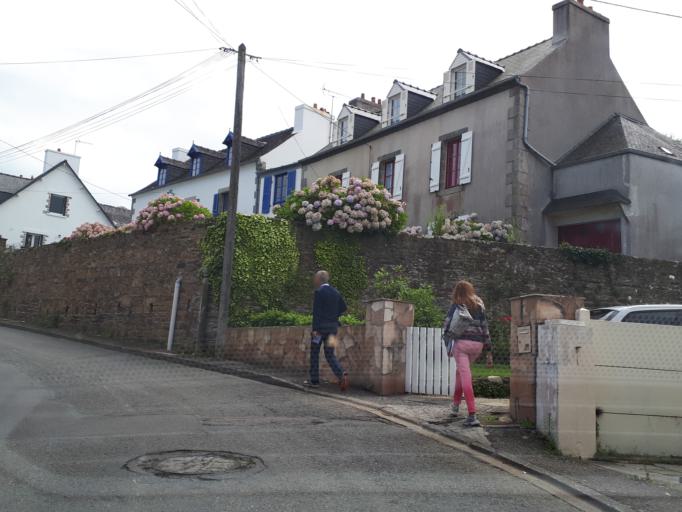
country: FR
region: Brittany
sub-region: Departement du Finistere
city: Carantec
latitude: 48.6711
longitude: -3.9181
